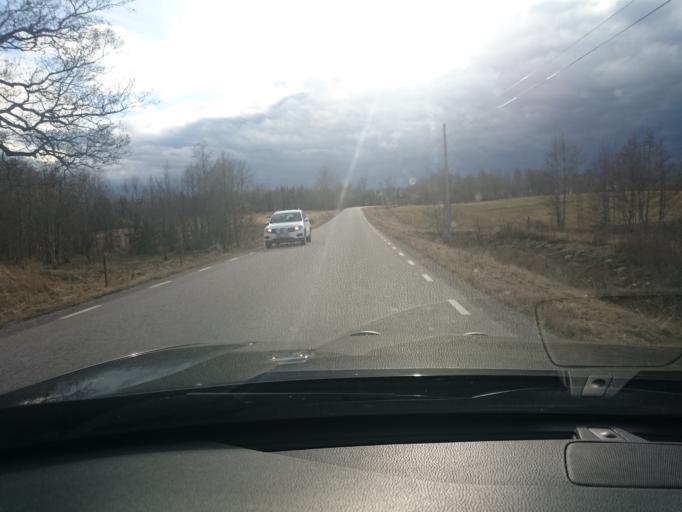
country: SE
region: Joenkoeping
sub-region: Vetlanda Kommun
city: Vetlanda
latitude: 57.3170
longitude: 15.1281
